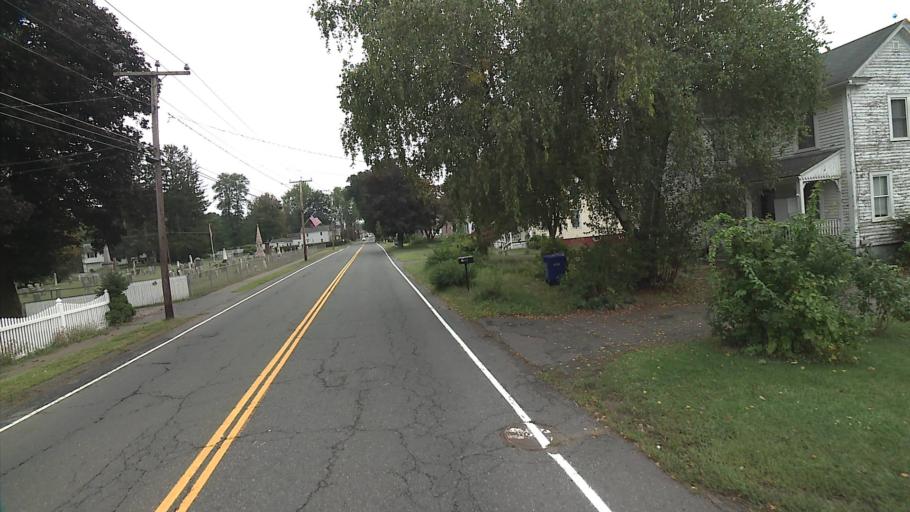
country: US
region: Connecticut
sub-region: Hartford County
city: Windsor Locks
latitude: 41.9337
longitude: -72.6178
